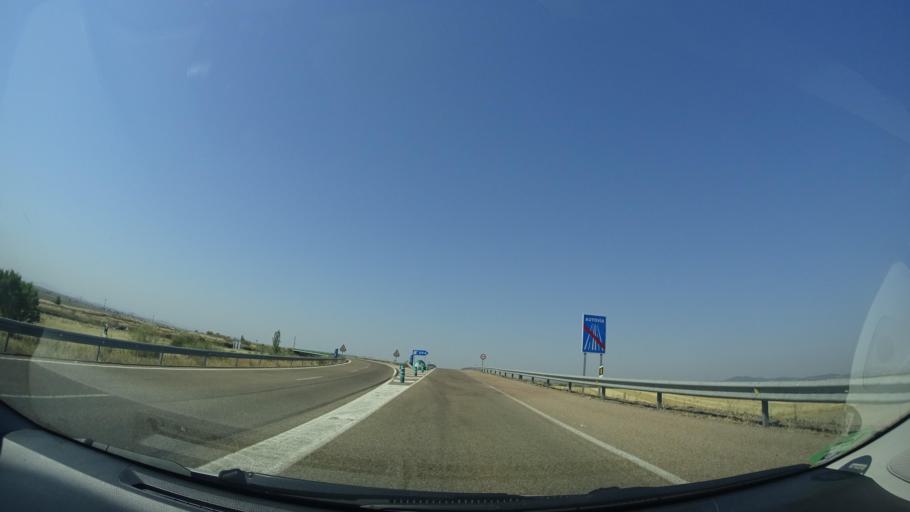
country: ES
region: Extremadura
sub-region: Provincia de Caceres
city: Miajadas
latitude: 39.1279
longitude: -5.9564
